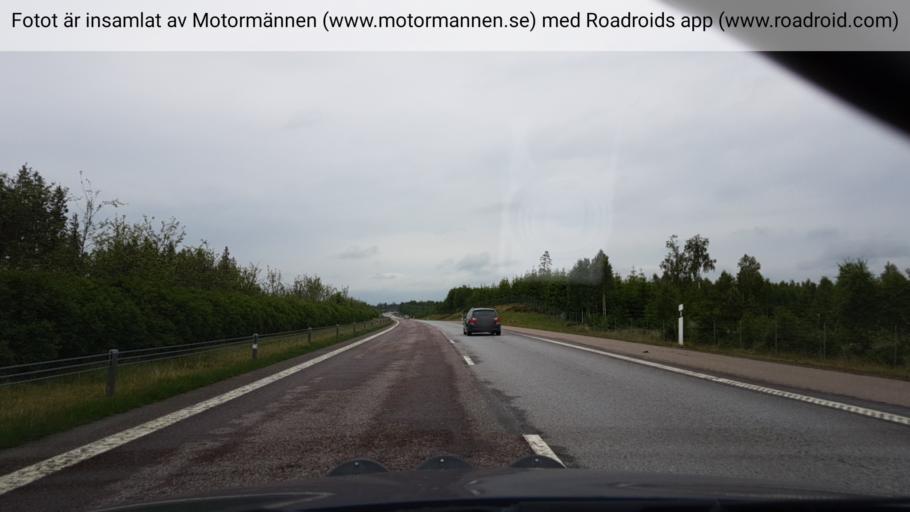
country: SE
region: Kronoberg
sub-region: Ljungby Kommun
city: Ljungby
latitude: 56.7081
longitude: 13.8397
